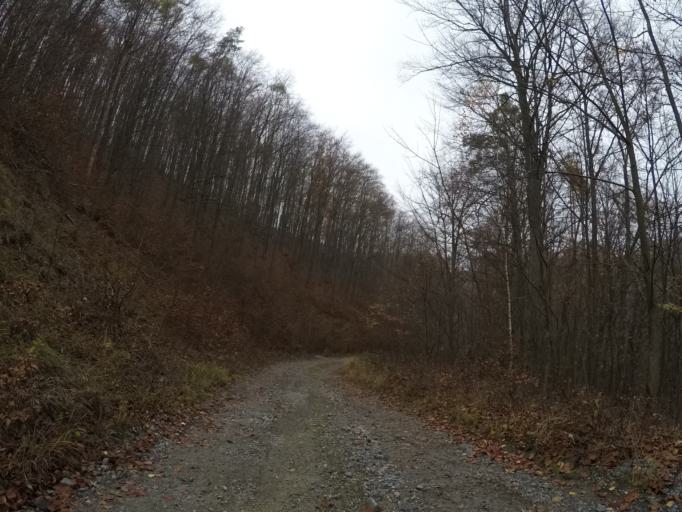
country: SK
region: Presovsky
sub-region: Okres Presov
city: Presov
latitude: 48.8903
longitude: 21.1992
